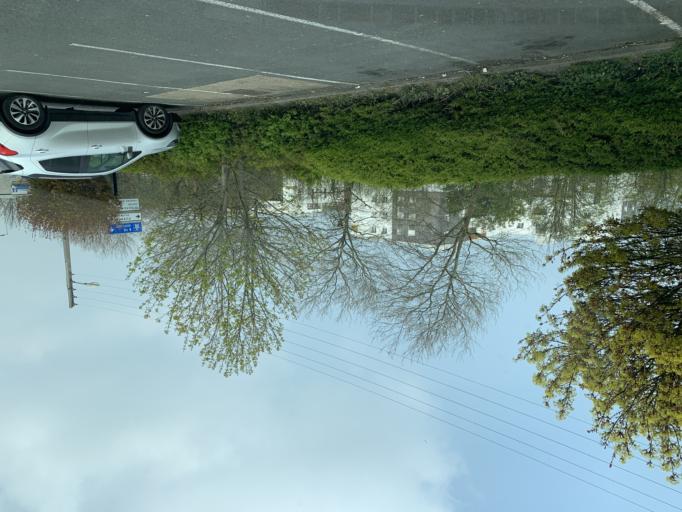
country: FR
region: Nord-Pas-de-Calais
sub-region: Departement du Nord
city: Coudekerque-Branche
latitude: 51.0363
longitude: 2.4126
